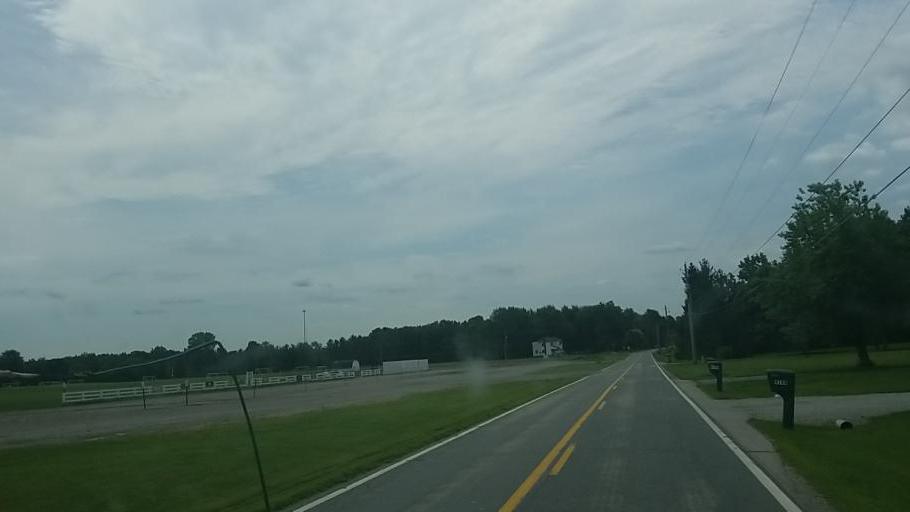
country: US
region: Ohio
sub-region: Delaware County
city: Sunbury
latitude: 40.1690
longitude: -82.8262
